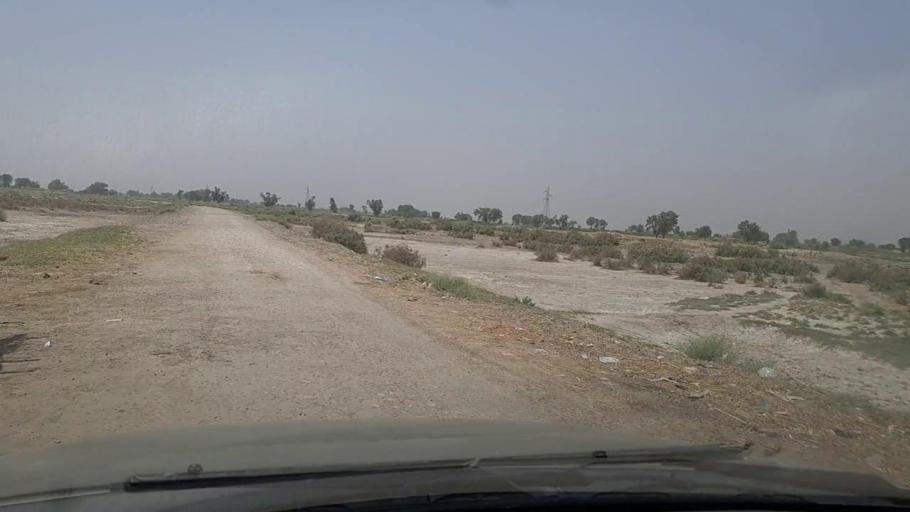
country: PK
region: Sindh
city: Ratodero
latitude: 27.7865
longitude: 68.2025
